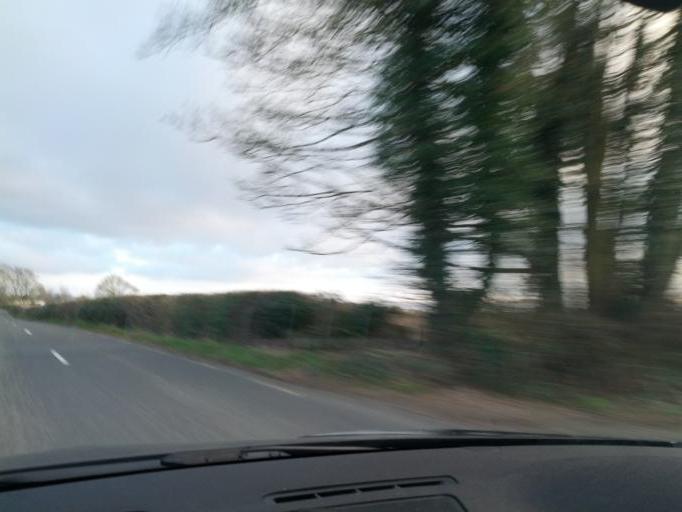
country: IE
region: Munster
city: Nenagh Bridge
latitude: 52.8897
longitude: -8.1998
